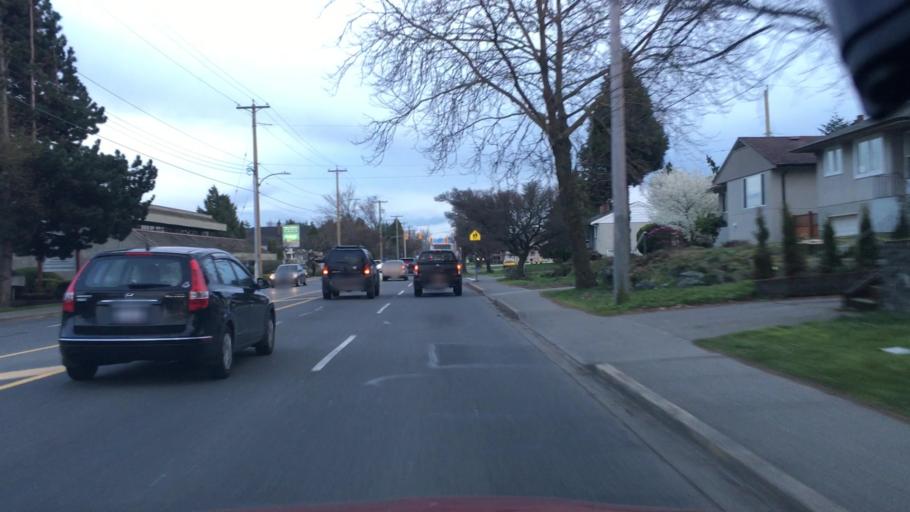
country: CA
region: British Columbia
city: Oak Bay
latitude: 48.4579
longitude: -123.3332
